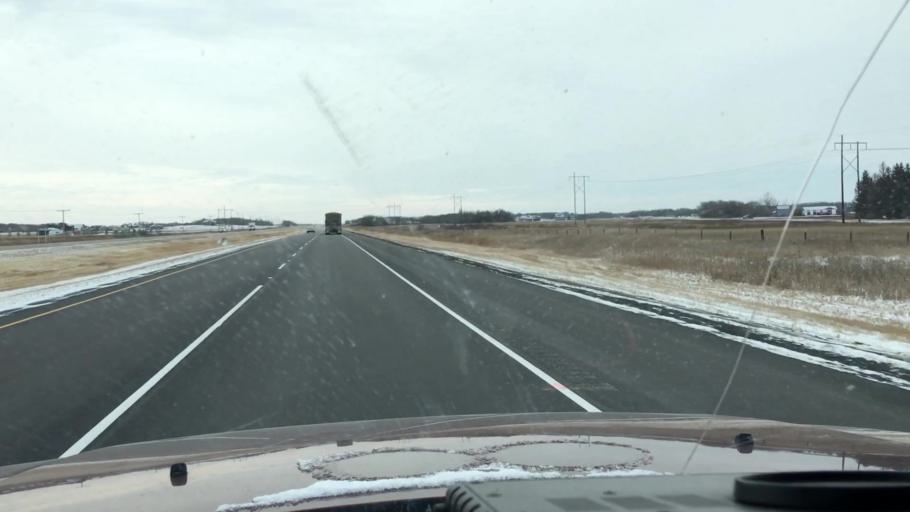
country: CA
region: Saskatchewan
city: Saskatoon
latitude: 51.9543
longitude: -106.5467
